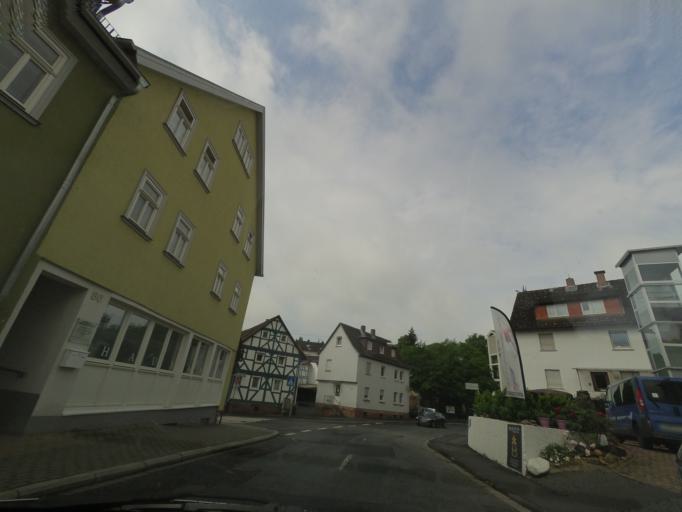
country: DE
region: Hesse
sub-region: Regierungsbezirk Giessen
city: Marburg an der Lahn
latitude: 50.8013
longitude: 8.7500
